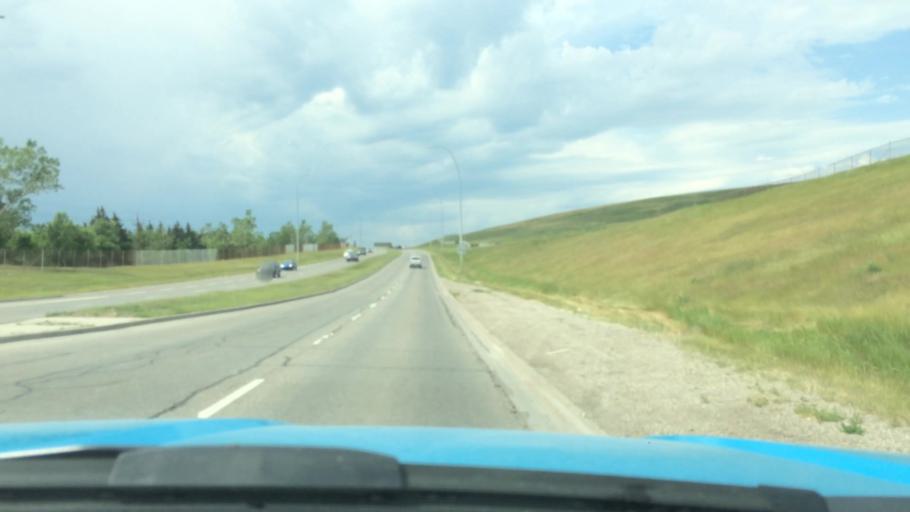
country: CA
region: Alberta
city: Calgary
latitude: 51.0970
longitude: -114.1164
